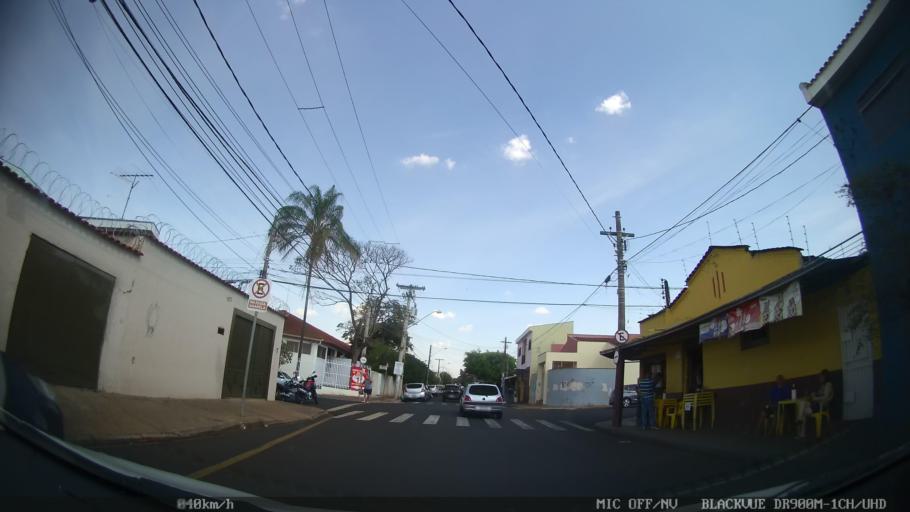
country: BR
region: Sao Paulo
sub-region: Ribeirao Preto
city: Ribeirao Preto
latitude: -21.1878
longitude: -47.8277
